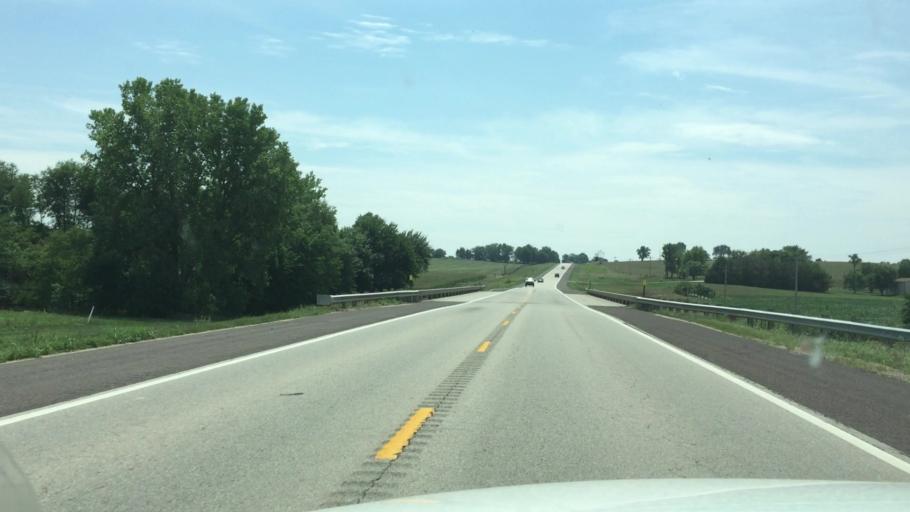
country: US
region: Kansas
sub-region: Jackson County
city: Holton
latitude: 39.5769
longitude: -95.7324
